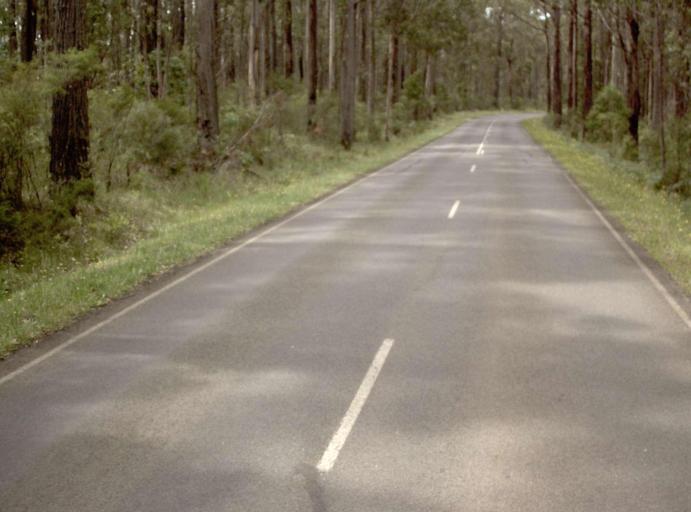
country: AU
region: Victoria
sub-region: Latrobe
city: Moe
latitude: -37.9915
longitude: 146.4095
